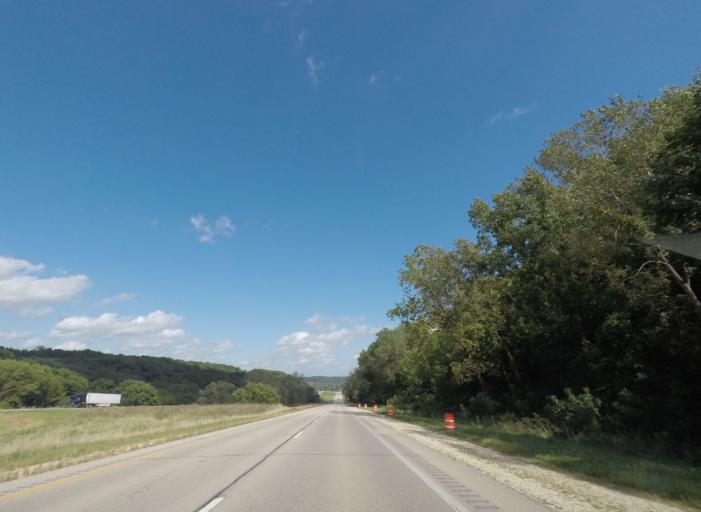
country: US
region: Iowa
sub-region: Dubuque County
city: Dubuque
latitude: 42.4176
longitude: -90.7176
